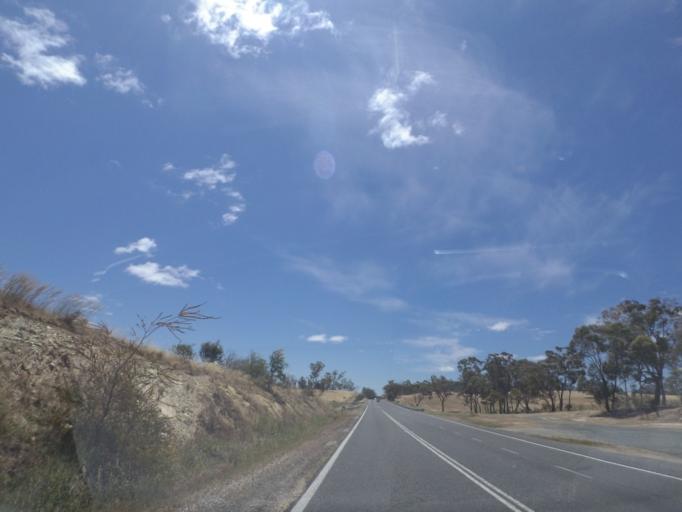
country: AU
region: Victoria
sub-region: Mount Alexander
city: Castlemaine
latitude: -37.2107
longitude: 144.1403
